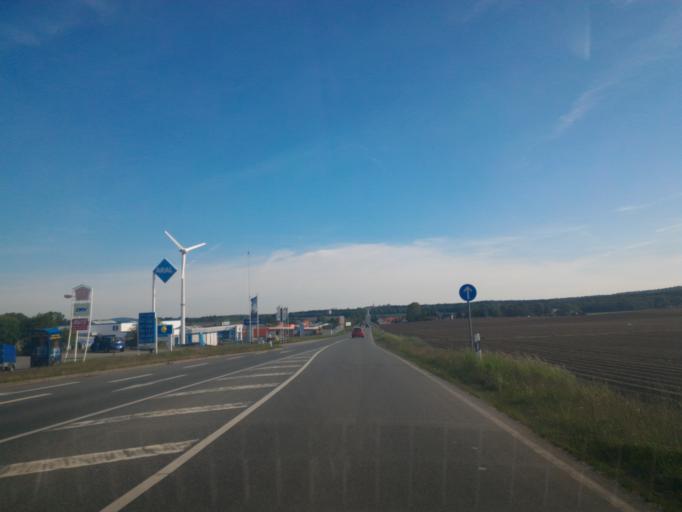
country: DE
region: Saxony
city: Neugersdorf
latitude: 50.9966
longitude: 14.6166
